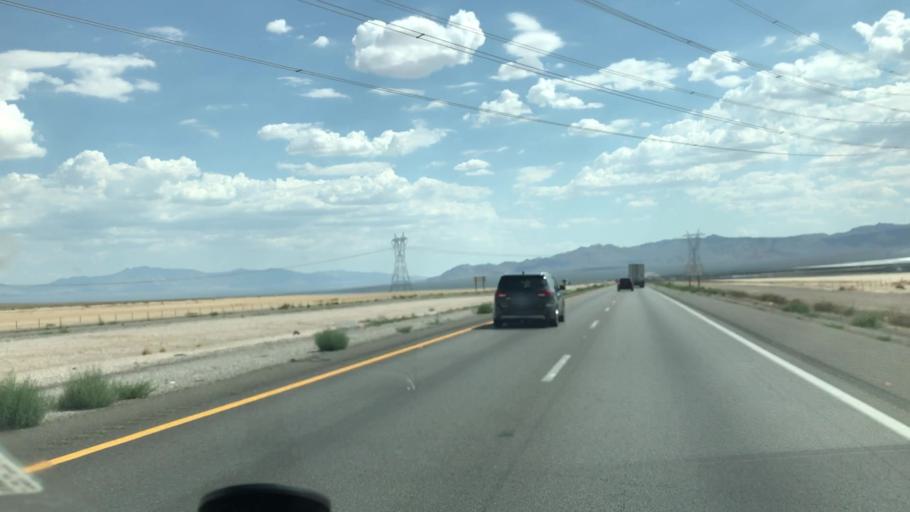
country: US
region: Nevada
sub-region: Clark County
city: Sandy Valley
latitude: 35.6013
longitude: -115.3942
